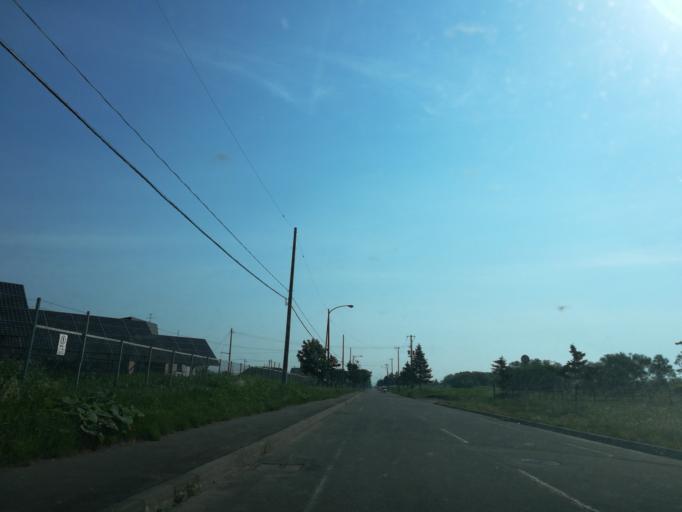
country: JP
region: Hokkaido
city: Iwamizawa
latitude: 43.1695
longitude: 141.7034
